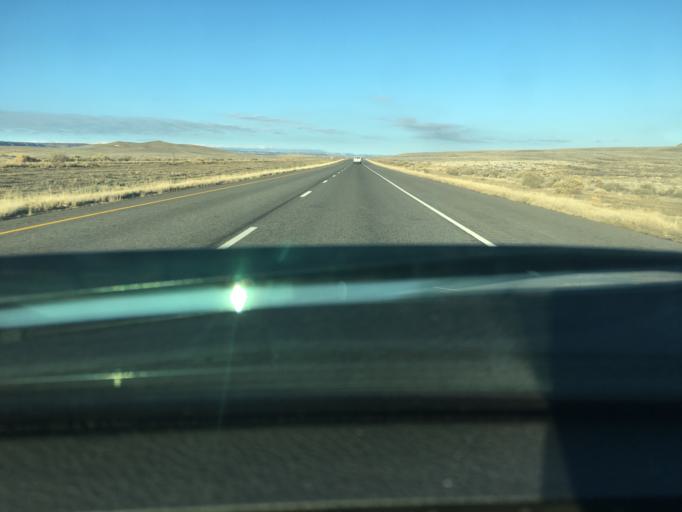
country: US
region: Colorado
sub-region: Delta County
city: Delta
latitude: 38.7647
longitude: -108.2099
